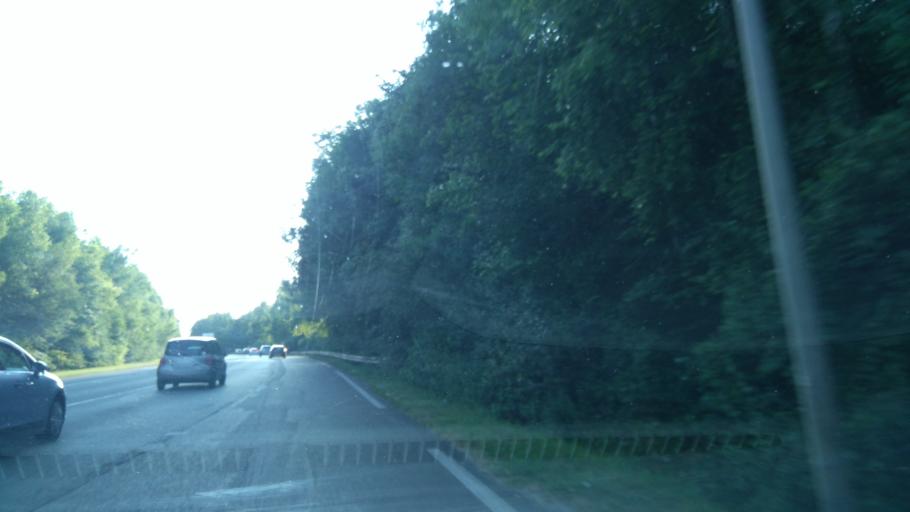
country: FR
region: Picardie
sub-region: Departement de l'Oise
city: Creil
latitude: 49.2457
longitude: 2.4662
